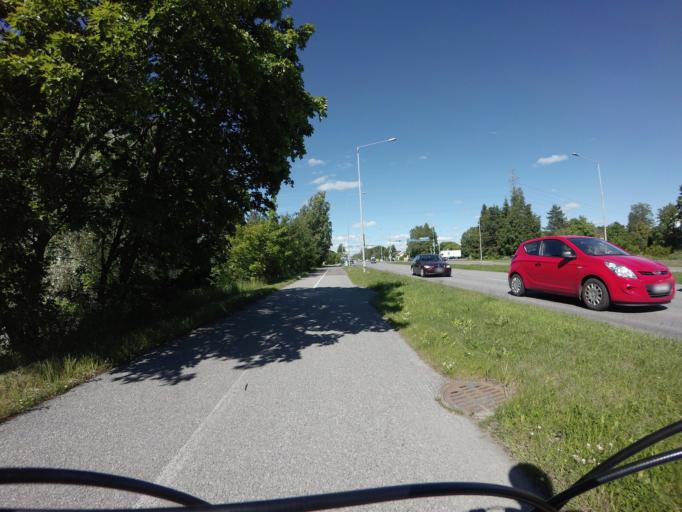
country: FI
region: Varsinais-Suomi
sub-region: Turku
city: Turku
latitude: 60.4745
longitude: 22.2652
